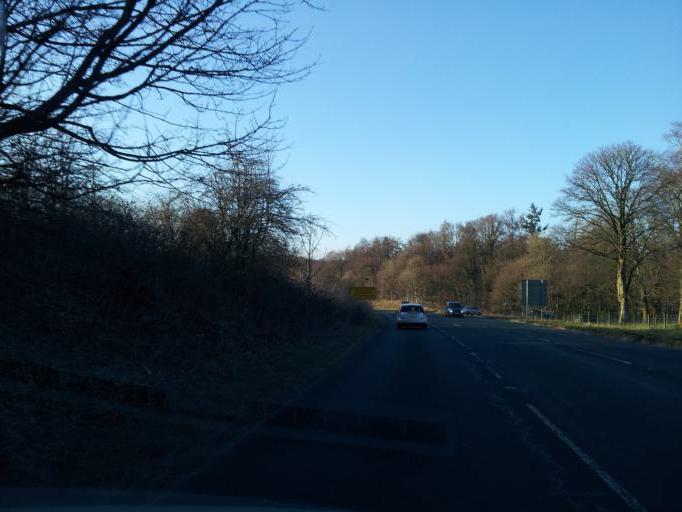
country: GB
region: England
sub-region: Cumbria
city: Kendal
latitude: 54.3486
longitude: -2.7766
